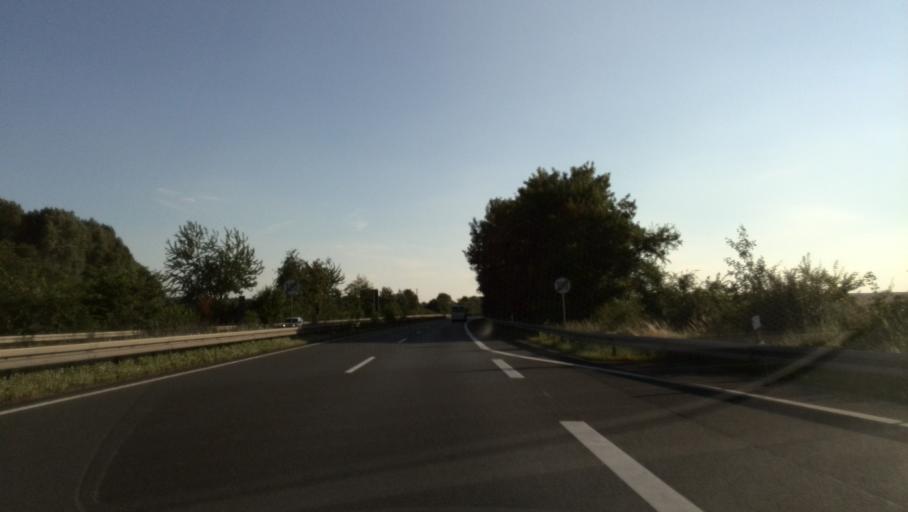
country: DE
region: Lower Saxony
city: Leiferde
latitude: 52.2072
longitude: 10.4866
